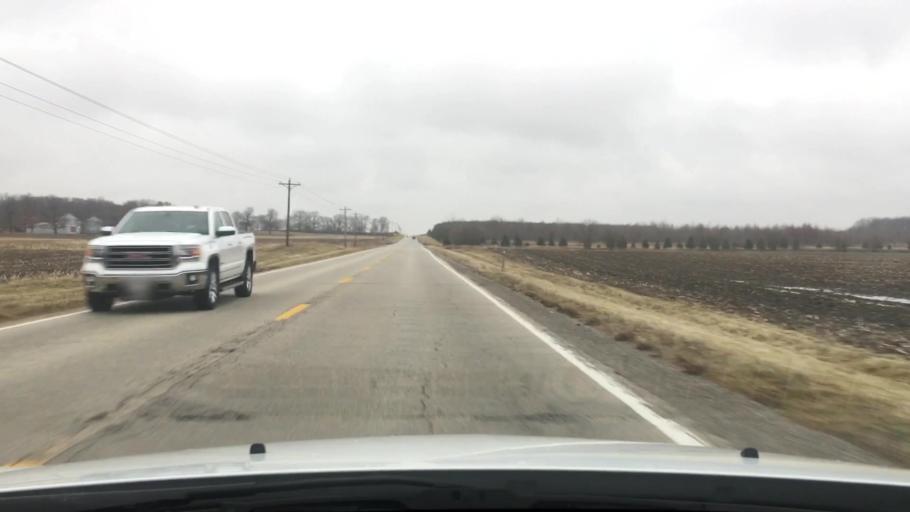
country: US
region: Illinois
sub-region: Iroquois County
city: Watseka
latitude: 40.8912
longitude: -87.6795
